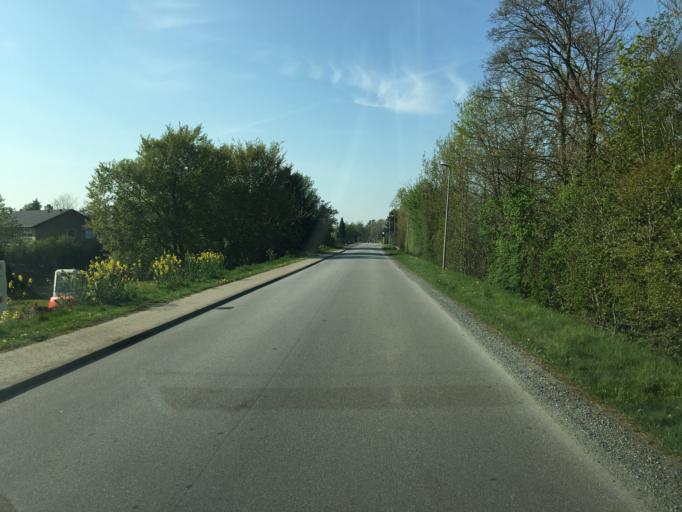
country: DK
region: South Denmark
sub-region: Haderslev Kommune
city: Vojens
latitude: 55.2449
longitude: 9.3167
